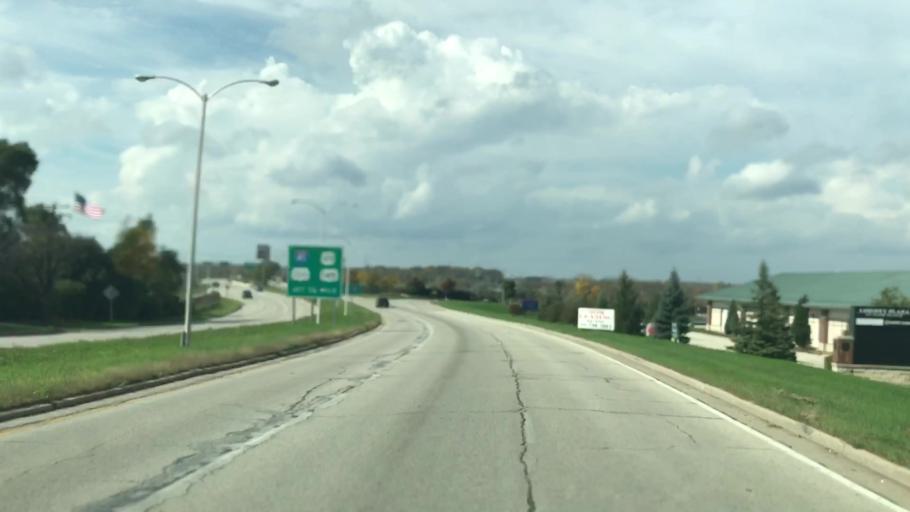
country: US
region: Wisconsin
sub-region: Waukesha County
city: Butler
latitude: 43.1484
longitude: -88.0466
